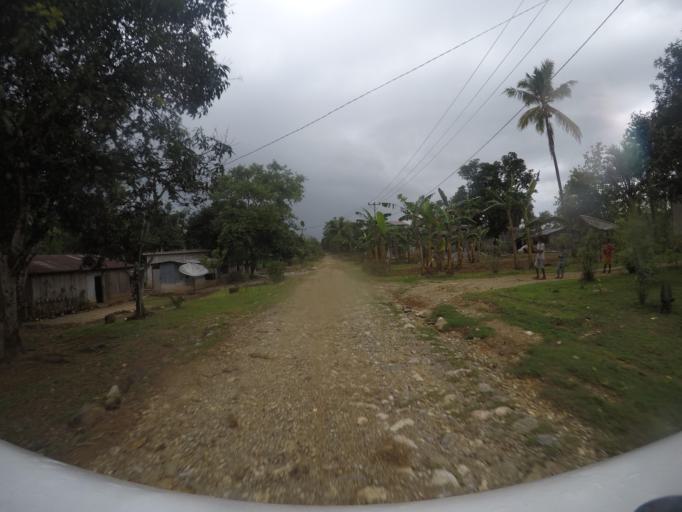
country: TL
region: Bobonaro
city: Maliana
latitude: -8.9604
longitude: 125.2138
